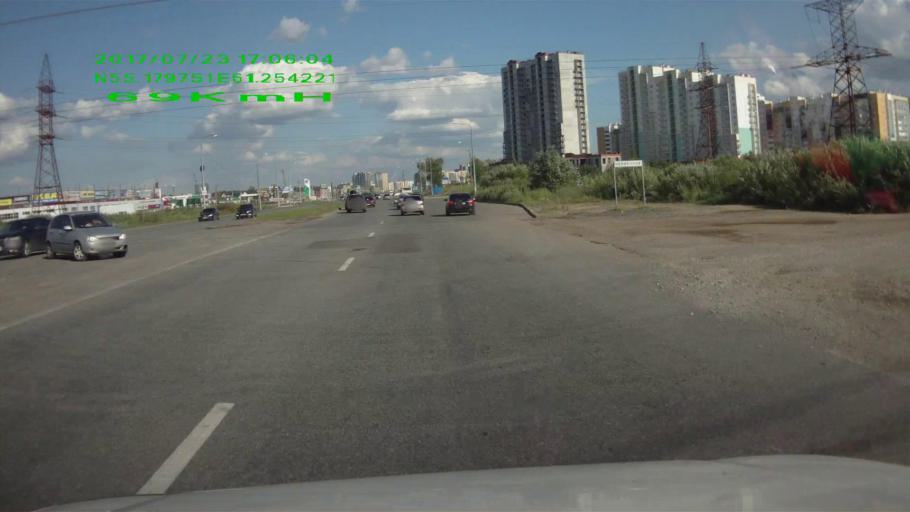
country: RU
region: Chelyabinsk
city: Roshchino
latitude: 55.1795
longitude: 61.2553
